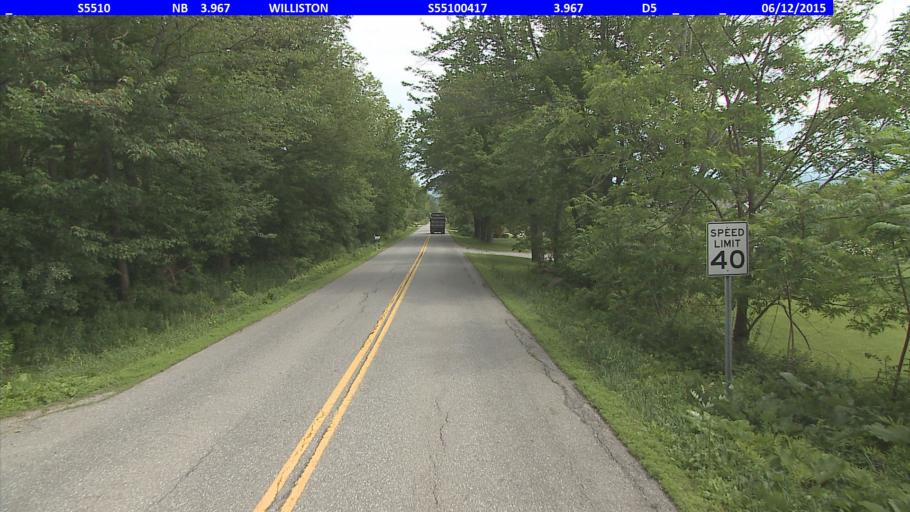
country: US
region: Vermont
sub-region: Chittenden County
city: Williston
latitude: 44.4263
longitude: -73.0768
